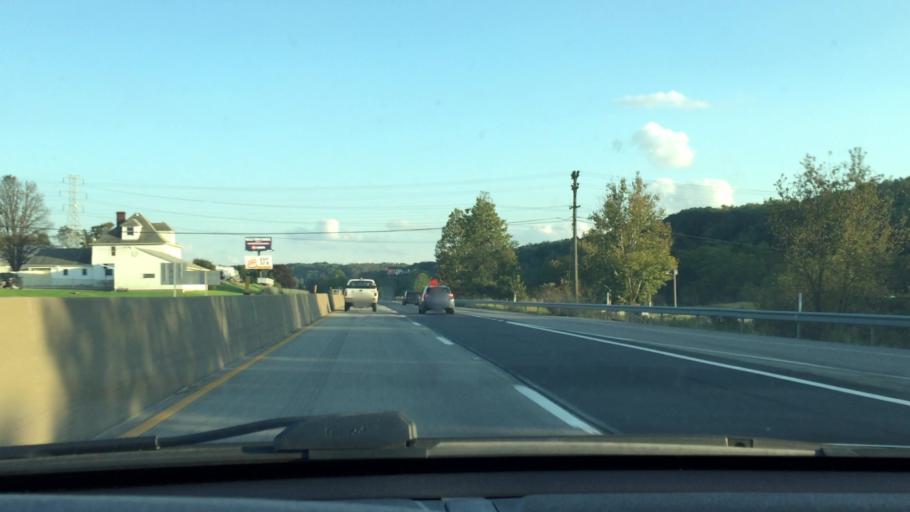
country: US
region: Pennsylvania
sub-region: Washington County
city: Bentleyville
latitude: 40.1490
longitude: -80.0307
